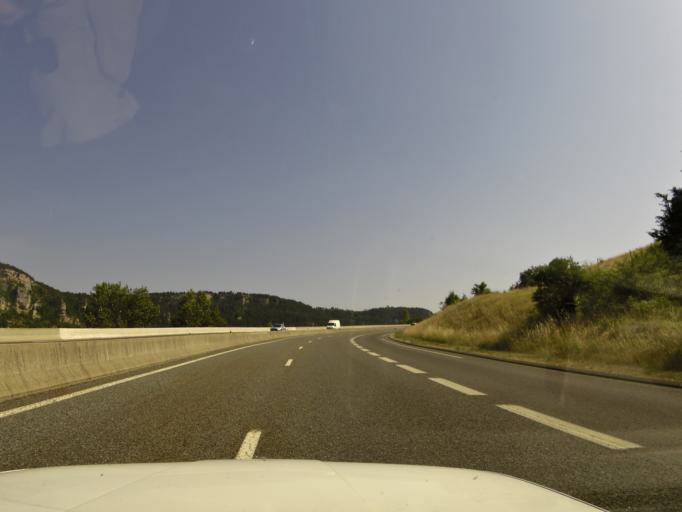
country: FR
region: Languedoc-Roussillon
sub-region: Departement de la Lozere
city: La Canourgue
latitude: 44.4208
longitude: 3.1841
